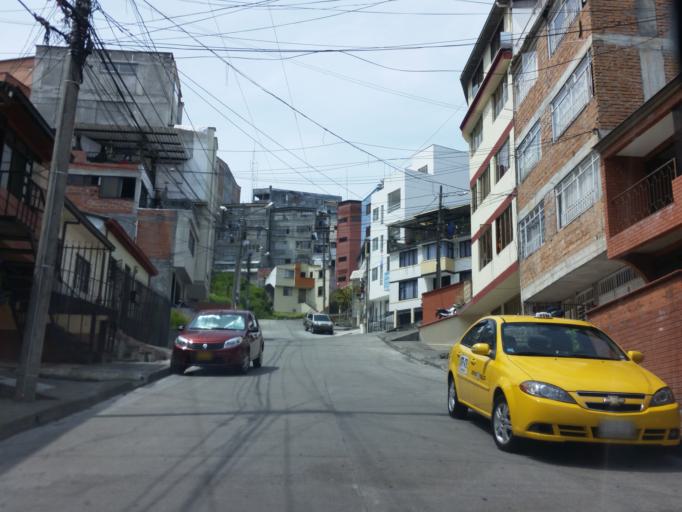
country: CO
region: Caldas
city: Manizales
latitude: 5.0727
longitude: -75.5232
